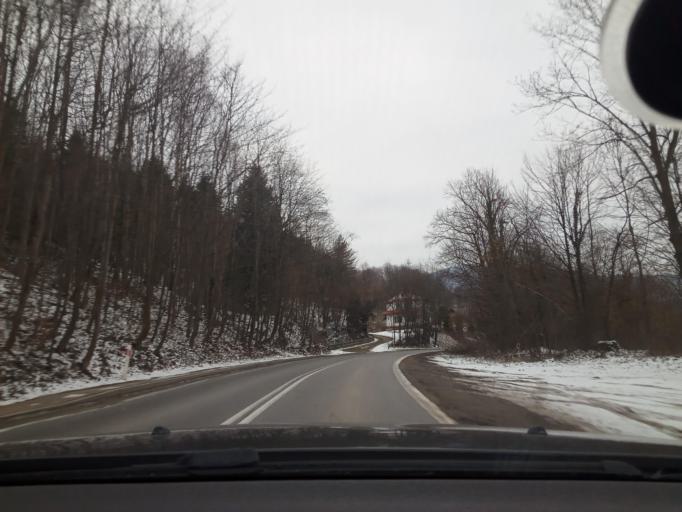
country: PL
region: Lesser Poland Voivodeship
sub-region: Powiat nowotarski
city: Kroscienko nad Dunajcem
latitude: 49.4755
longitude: 20.4200
